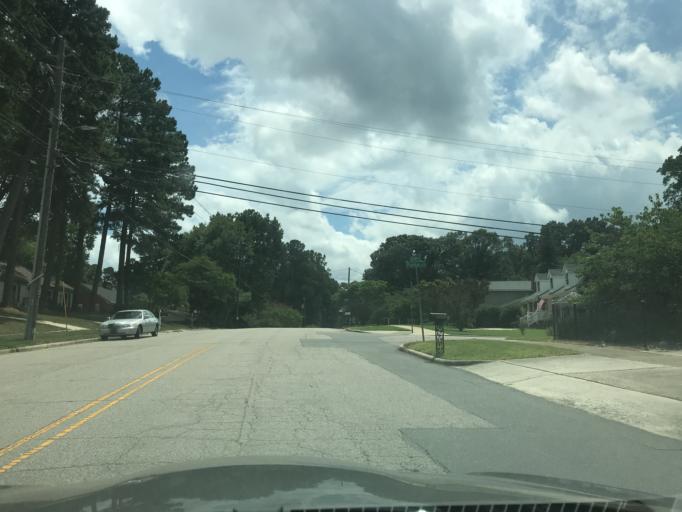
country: US
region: North Carolina
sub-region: Wake County
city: West Raleigh
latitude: 35.8486
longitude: -78.6214
